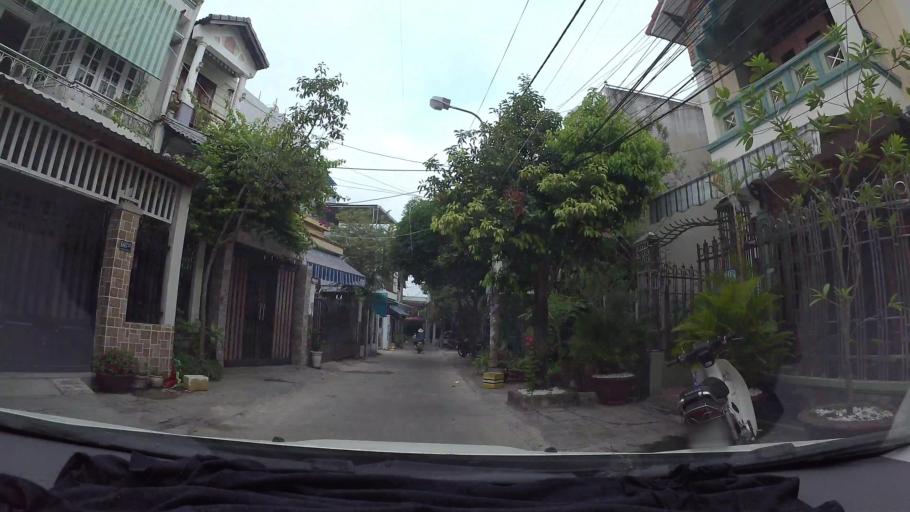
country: VN
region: Da Nang
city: Thanh Khe
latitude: 16.0710
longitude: 108.1863
